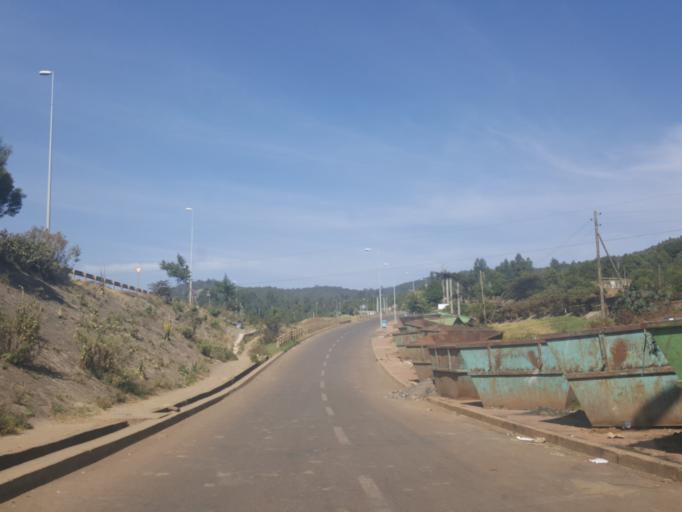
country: ET
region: Adis Abeba
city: Addis Ababa
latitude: 9.0685
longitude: 38.7242
